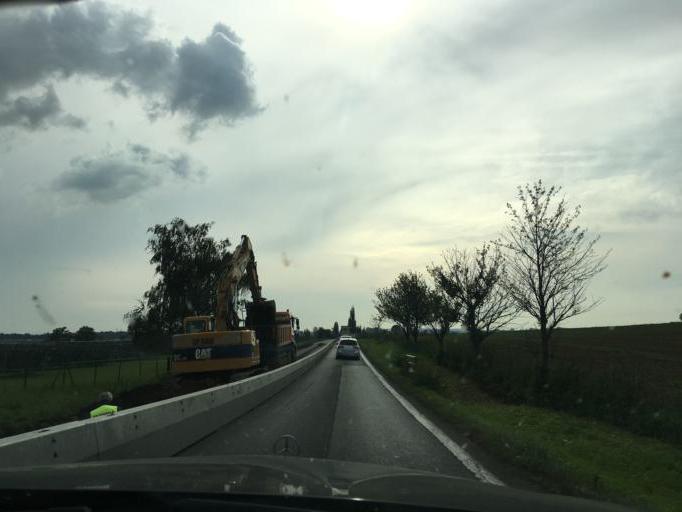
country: CZ
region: Kralovehradecky
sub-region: Okres Hradec Kralove
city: Smirice
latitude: 50.2974
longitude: 15.8436
